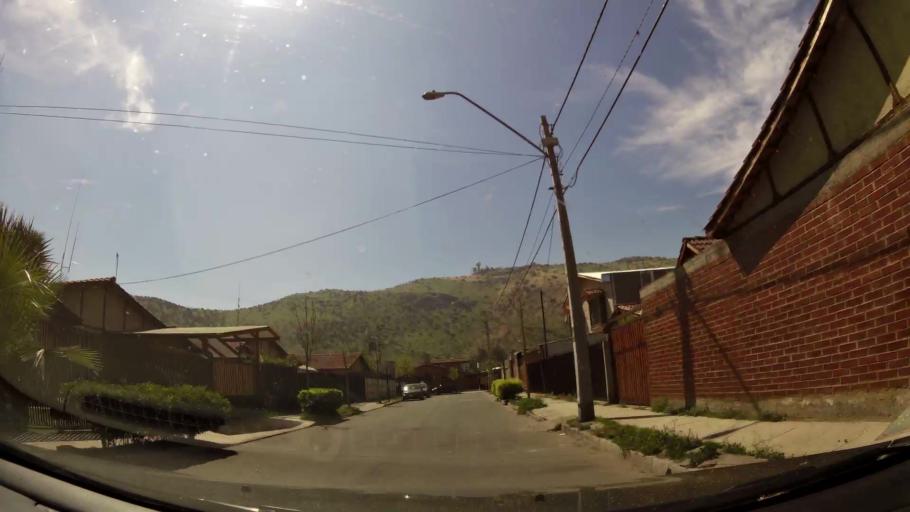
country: CL
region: Santiago Metropolitan
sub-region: Provincia de Santiago
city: Lo Prado
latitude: -33.3959
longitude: -70.7470
